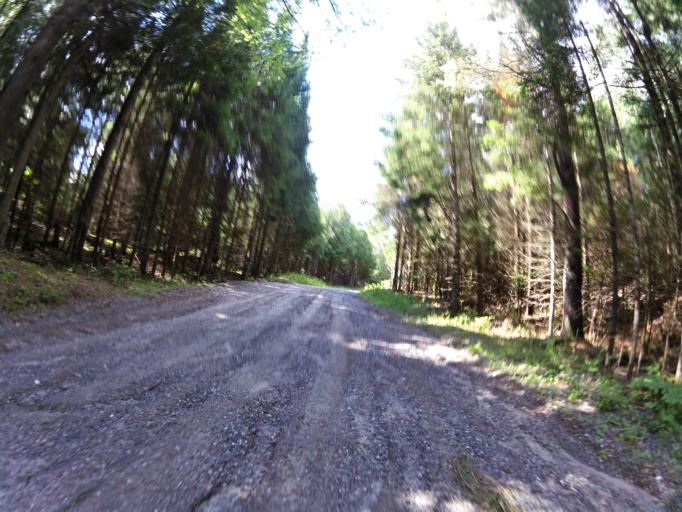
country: CA
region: Ontario
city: Perth
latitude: 45.0759
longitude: -76.4667
